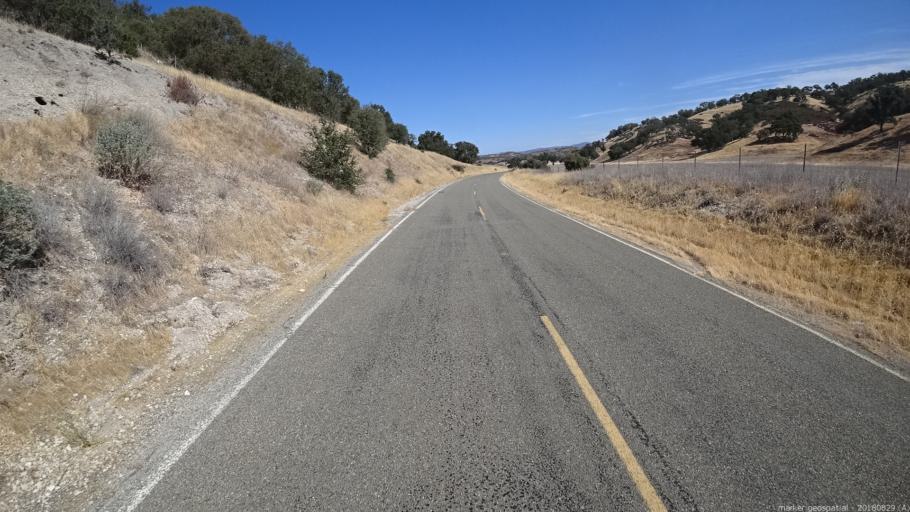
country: US
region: California
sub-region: San Luis Obispo County
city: Lake Nacimiento
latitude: 35.8780
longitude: -121.0662
